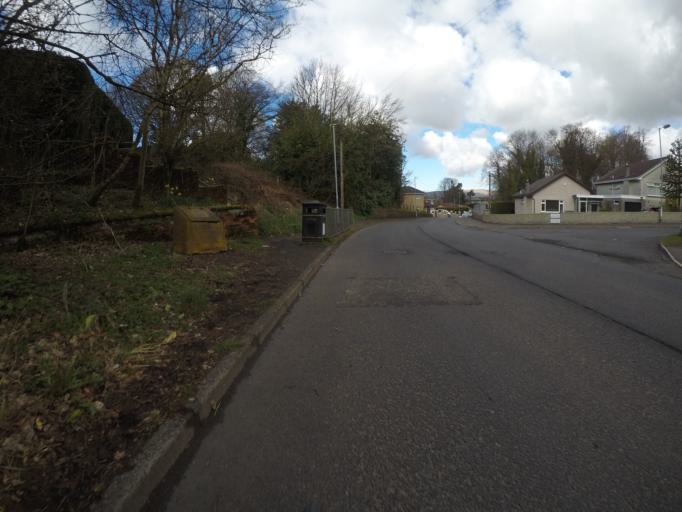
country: GB
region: Scotland
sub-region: North Ayrshire
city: Beith
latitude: 55.7474
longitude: -4.6355
